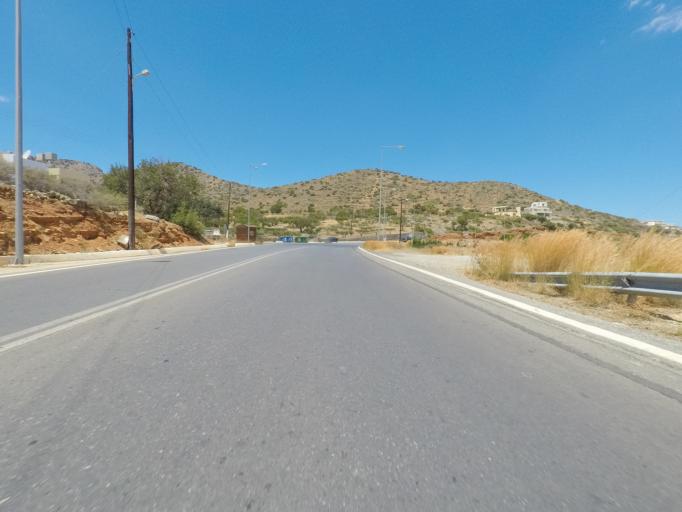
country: GR
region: Crete
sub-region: Nomos Lasithiou
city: Skhisma
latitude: 35.2299
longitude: 25.7236
